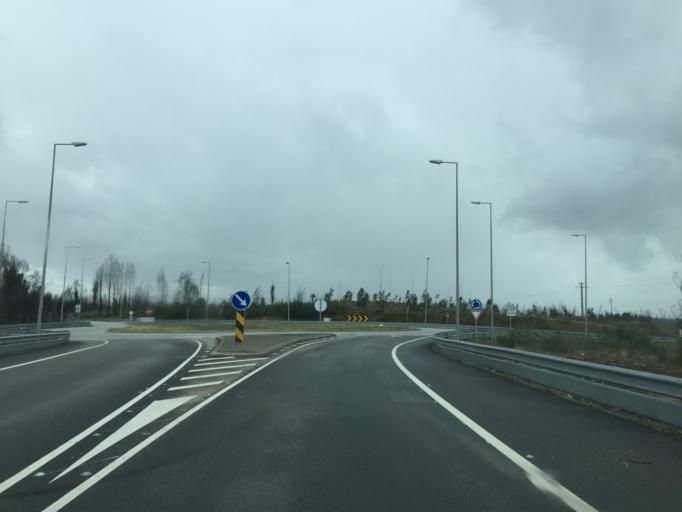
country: PT
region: Coimbra
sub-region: Tabua
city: Tabua
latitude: 40.3277
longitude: -7.9616
